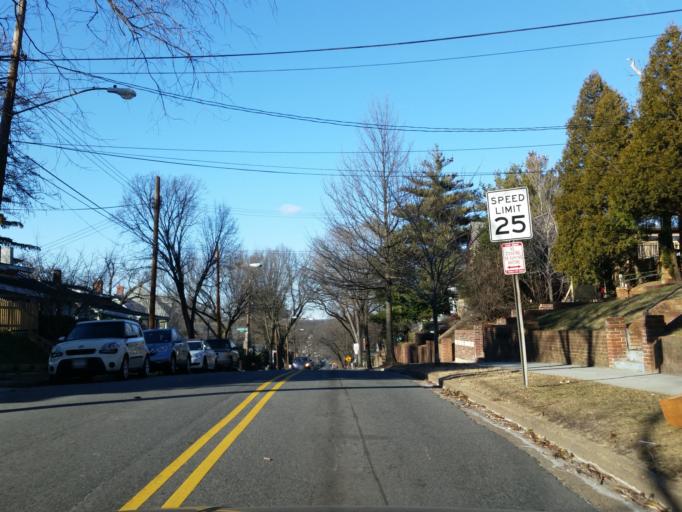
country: US
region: Maryland
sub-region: Prince George's County
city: Mount Rainier
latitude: 38.9294
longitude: -76.9793
